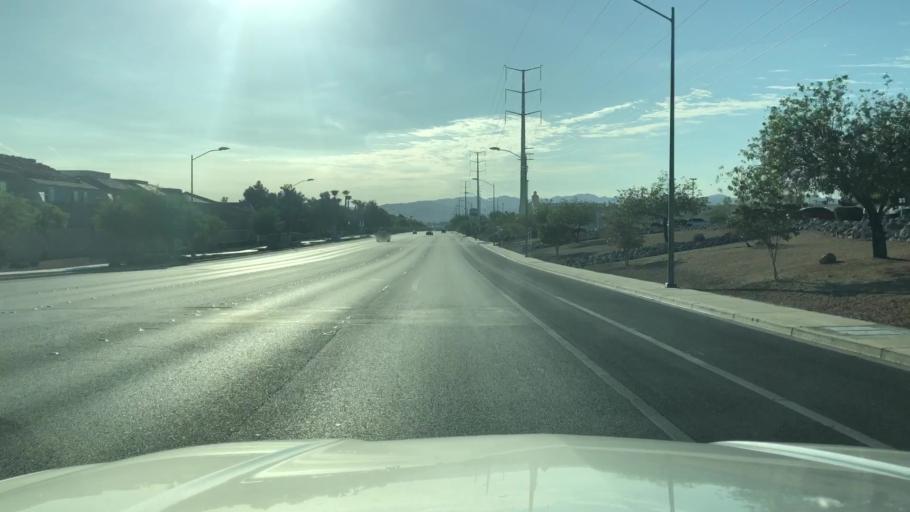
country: US
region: Nevada
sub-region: Clark County
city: Whitney
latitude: 36.0417
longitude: -115.0440
